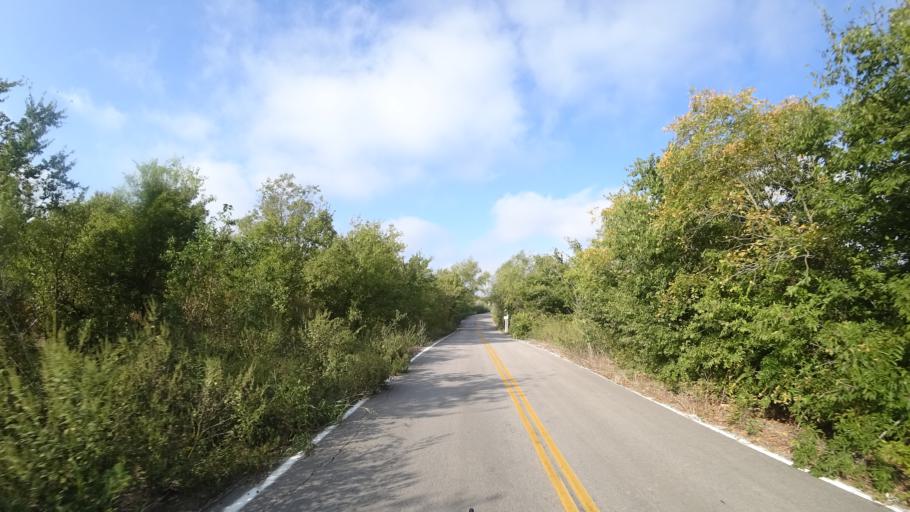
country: US
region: Texas
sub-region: Travis County
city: Manor
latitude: 30.3653
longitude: -97.6195
